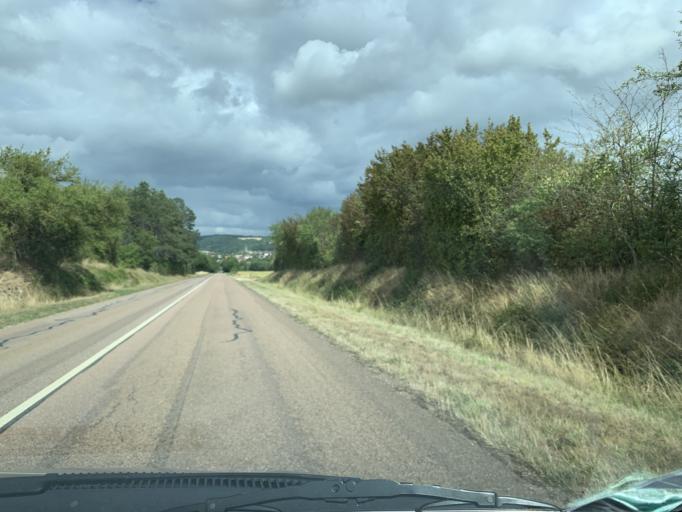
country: FR
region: Bourgogne
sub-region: Departement de la Nievre
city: Clamecy
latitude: 47.4438
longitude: 3.4963
